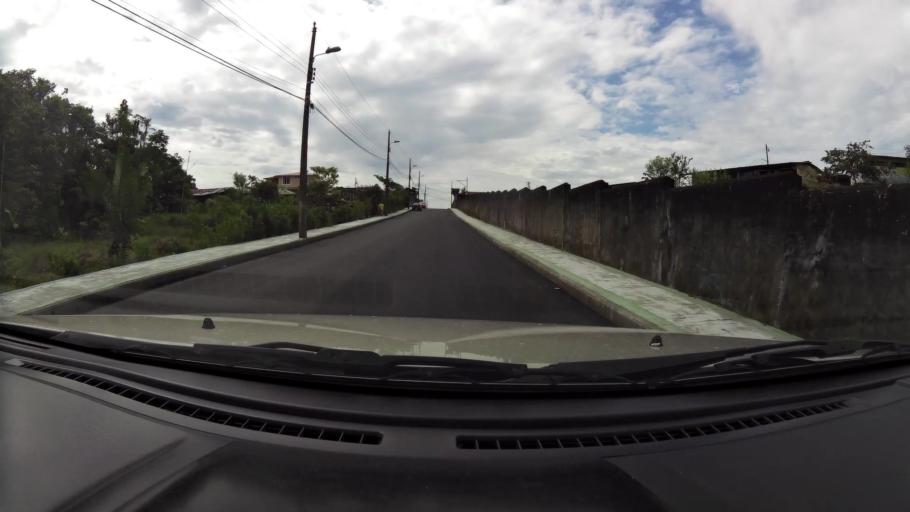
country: EC
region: Pastaza
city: Puyo
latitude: -1.4926
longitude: -77.9960
